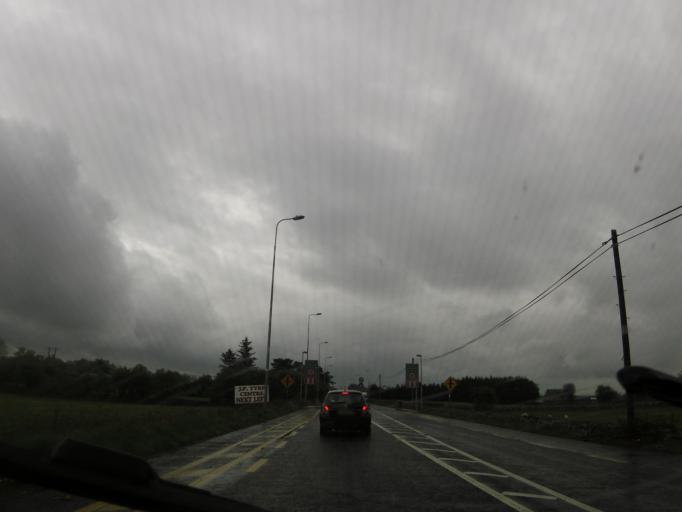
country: IE
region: Connaught
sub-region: County Galway
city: Claregalway
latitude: 53.3922
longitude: -8.9141
